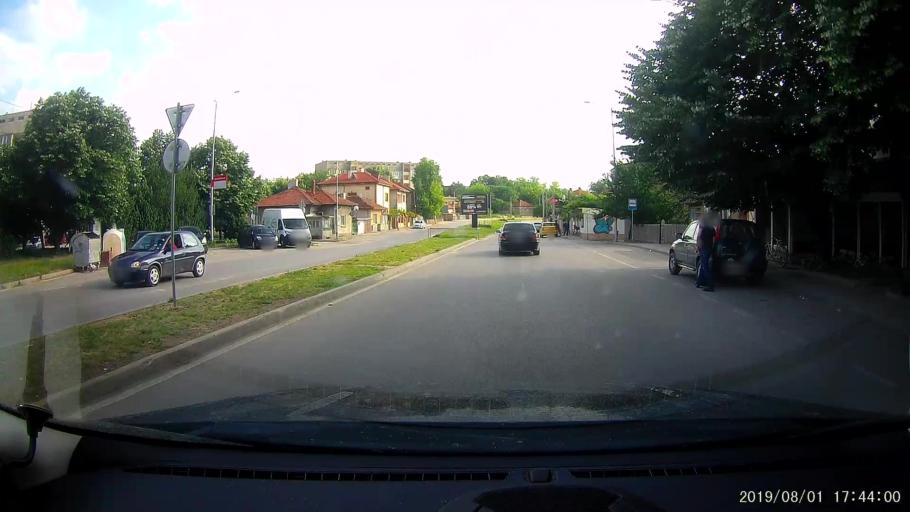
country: BG
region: Silistra
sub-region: Obshtina Silistra
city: Silistra
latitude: 44.1118
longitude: 27.2721
